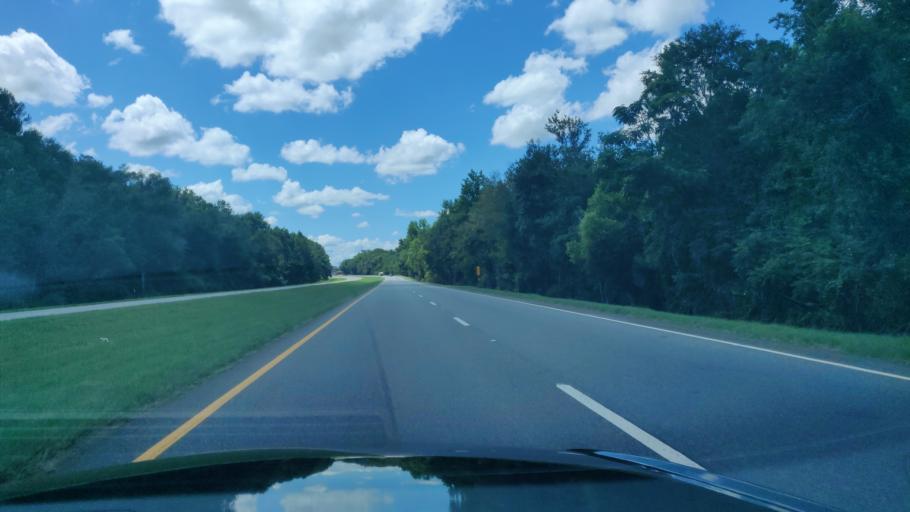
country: US
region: Georgia
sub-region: Terrell County
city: Dawson
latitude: 31.7323
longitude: -84.3673
